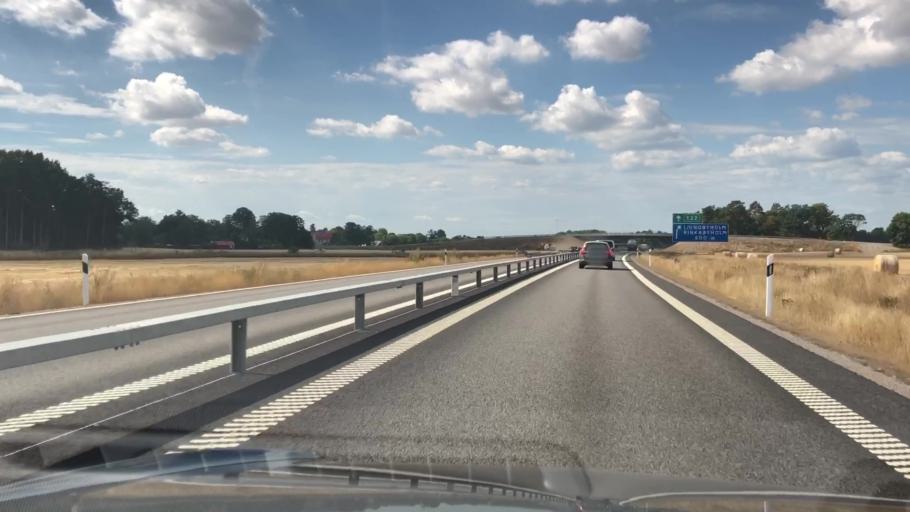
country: SE
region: Kalmar
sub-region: Kalmar Kommun
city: Rinkabyholm
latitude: 56.6439
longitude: 16.2293
